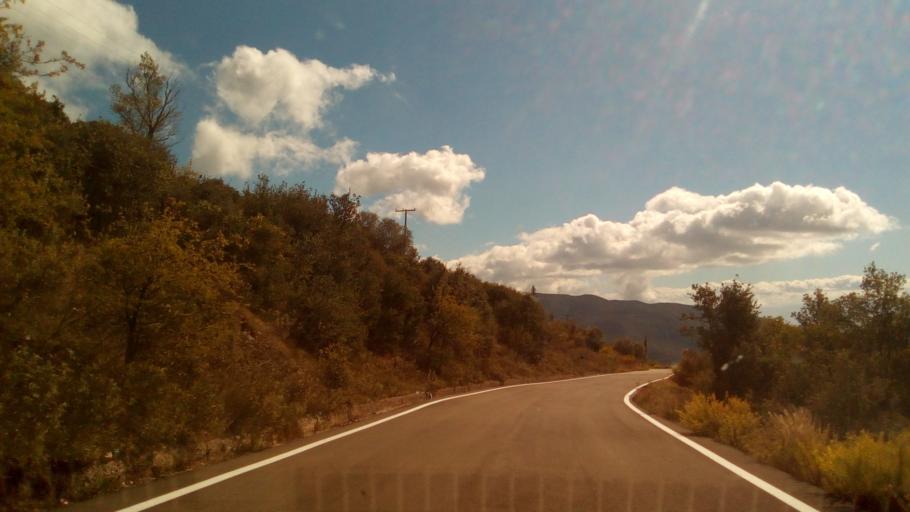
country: GR
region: West Greece
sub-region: Nomos Aitolias kai Akarnanias
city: Nafpaktos
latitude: 38.4840
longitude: 21.8553
